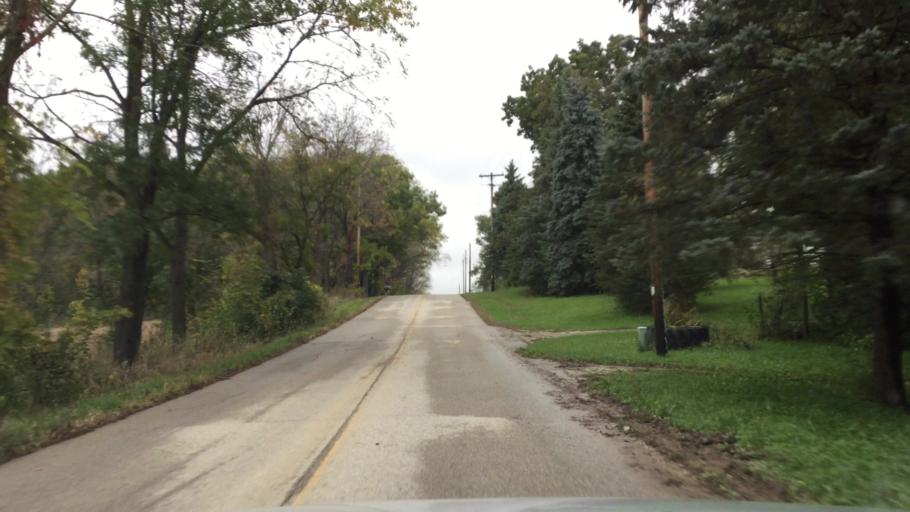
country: US
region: Wisconsin
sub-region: Racine County
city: Eagle Lake
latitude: 42.7472
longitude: -88.1553
